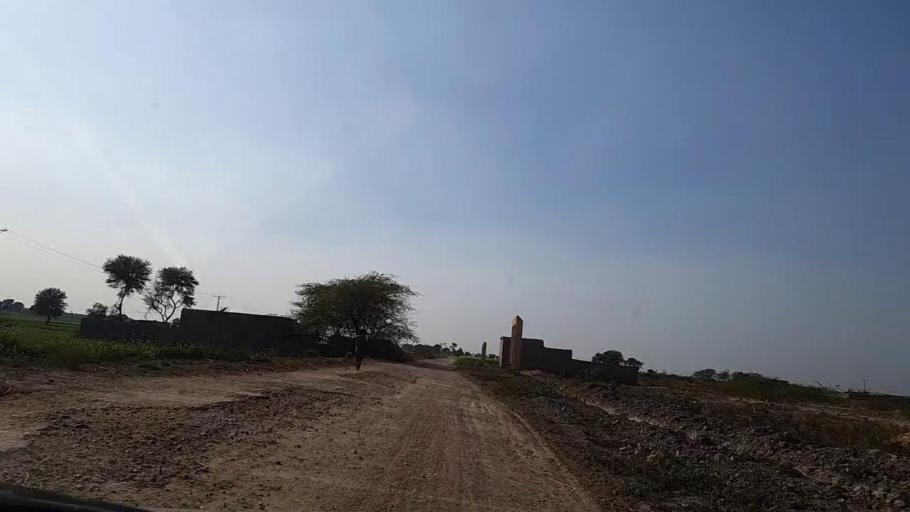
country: PK
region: Sindh
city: Sakrand
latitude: 26.1279
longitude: 68.2675
